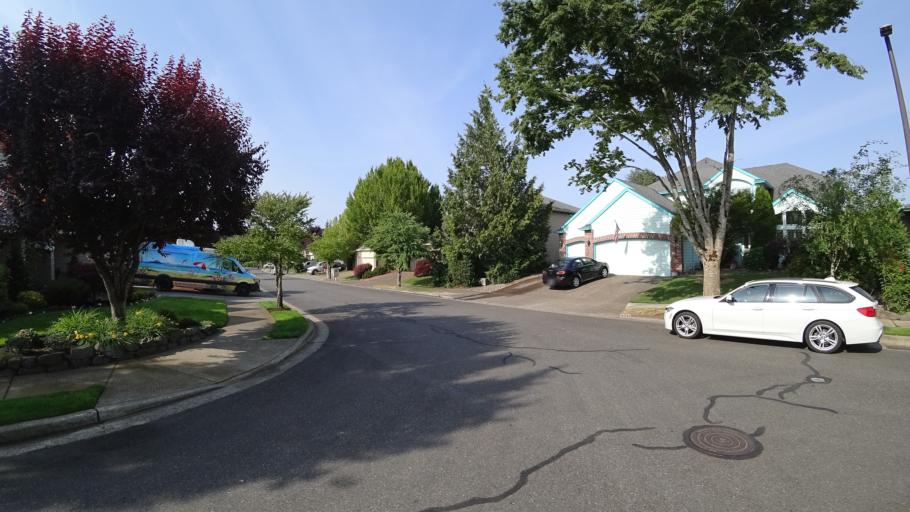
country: US
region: Oregon
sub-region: Clackamas County
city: Happy Valley
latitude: 45.4523
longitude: -122.5188
